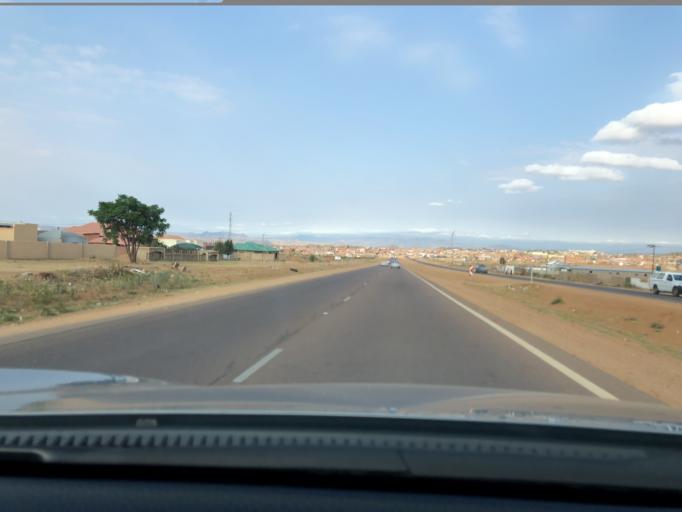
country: ZA
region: Limpopo
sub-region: Capricorn District Municipality
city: Mankoeng
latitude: -23.8878
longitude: 29.6783
